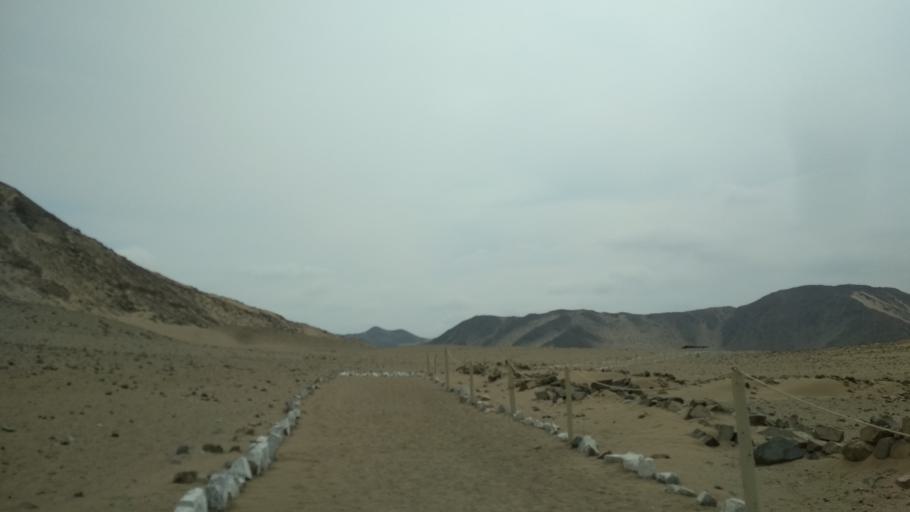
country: PE
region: Lima
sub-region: Huaura
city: Vegueta
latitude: -10.8928
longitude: -77.5171
